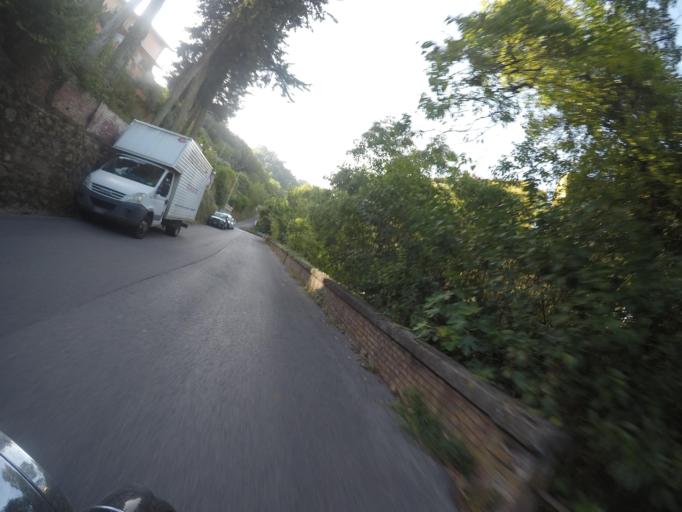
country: IT
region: Tuscany
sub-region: Provincia di Massa-Carrara
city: Carrara
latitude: 44.0816
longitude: 10.0939
